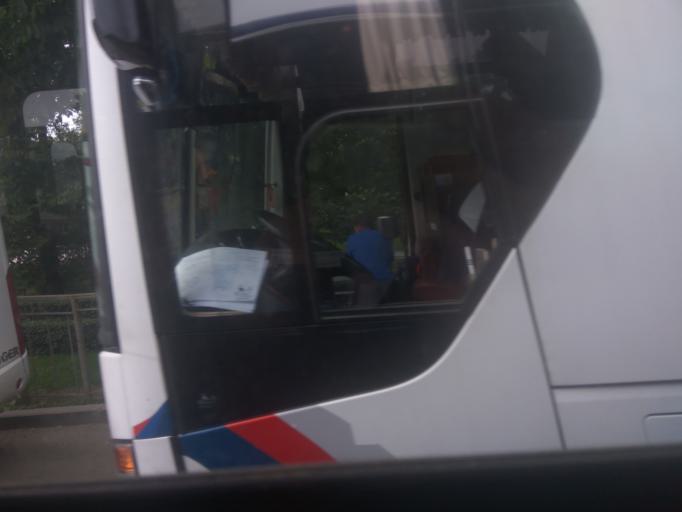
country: RU
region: Primorskiy
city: Vladivostok
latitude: 43.1635
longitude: 131.9131
